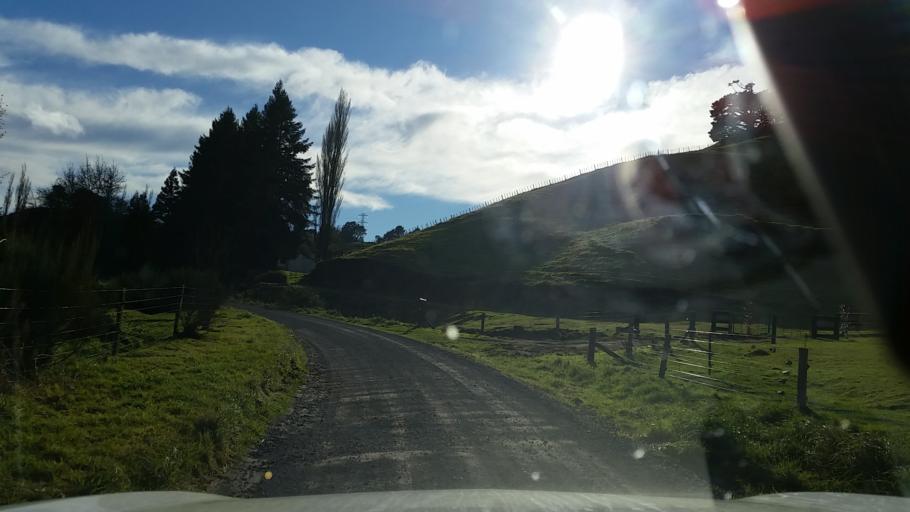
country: NZ
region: Waikato
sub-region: South Waikato District
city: Tokoroa
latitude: -38.3689
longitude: 176.0890
